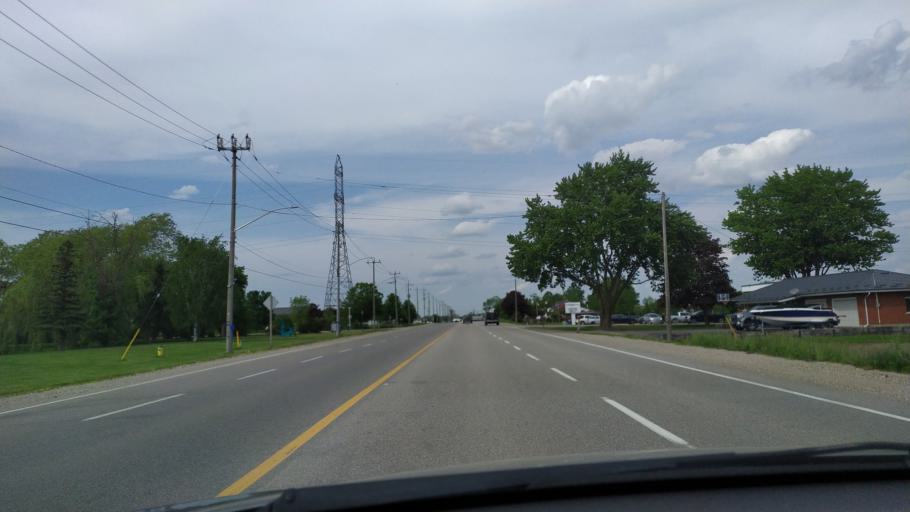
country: CA
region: Ontario
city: Stratford
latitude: 43.3441
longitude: -81.0059
